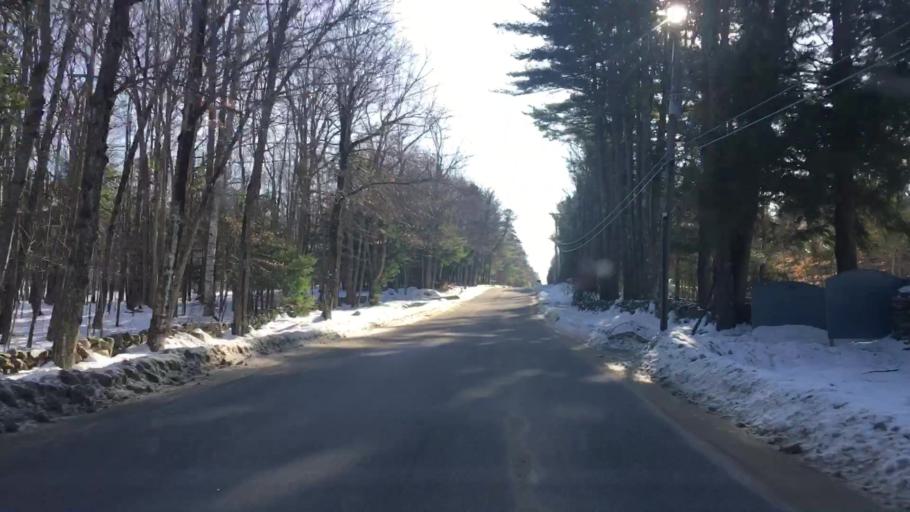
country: US
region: Maine
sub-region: Oxford County
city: Paris
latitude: 44.2763
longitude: -70.5078
